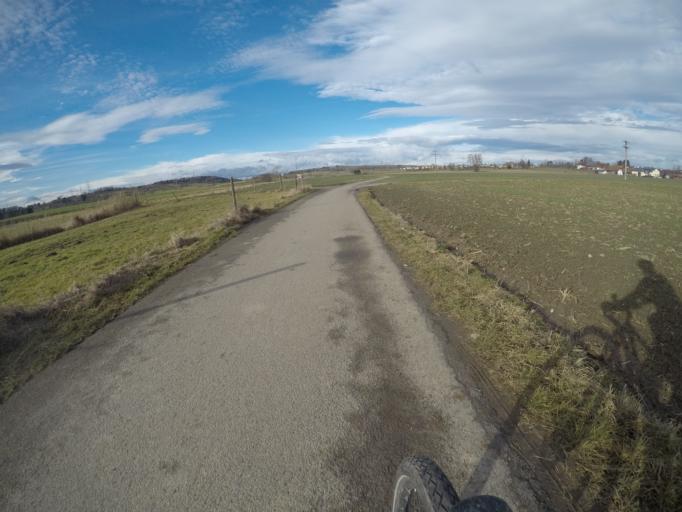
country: DE
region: Baden-Wuerttemberg
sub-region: Regierungsbezirk Stuttgart
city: Ehningen
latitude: 48.6840
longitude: 8.9516
